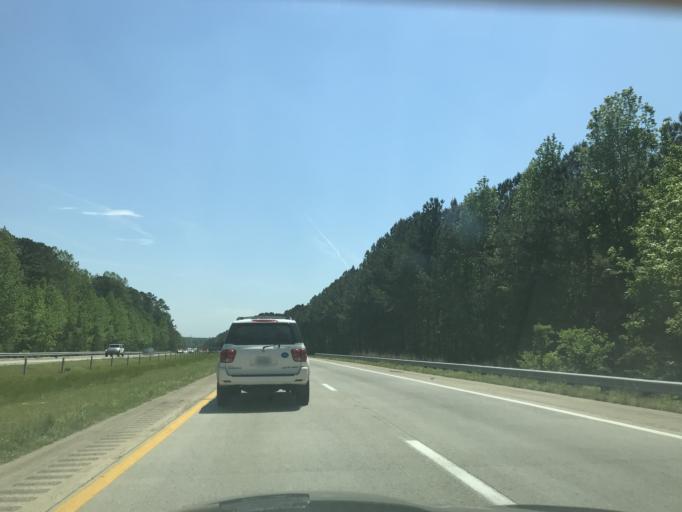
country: US
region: North Carolina
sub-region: Wake County
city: Garner
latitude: 35.5807
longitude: -78.5765
